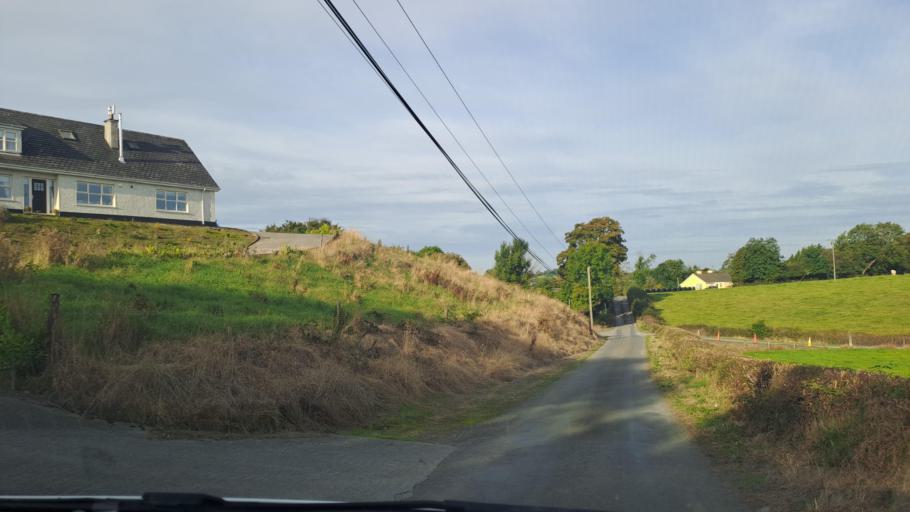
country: IE
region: Ulster
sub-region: An Cabhan
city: Bailieborough
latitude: 53.9895
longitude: -6.8840
